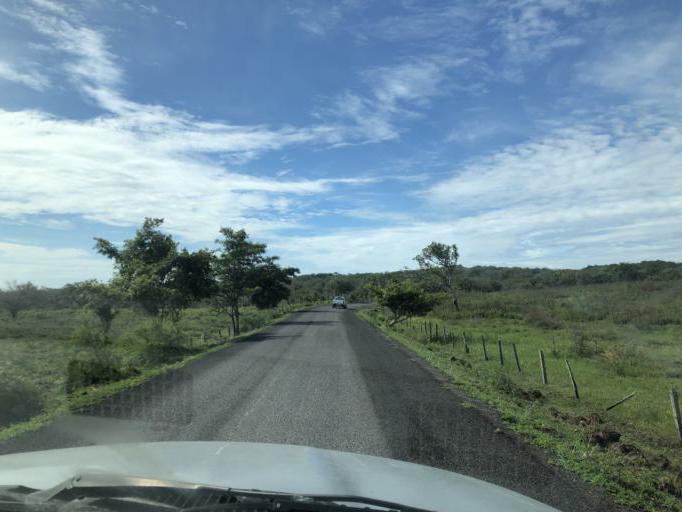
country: MX
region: Veracruz
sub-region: Alto Lucero de Gutierrez Barrios
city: Palma Sola
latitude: 19.7855
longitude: -96.5528
